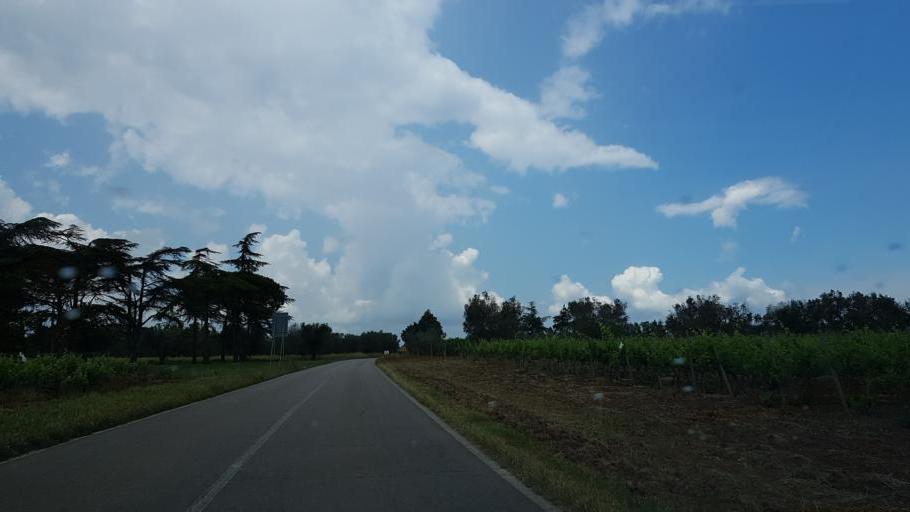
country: IT
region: Apulia
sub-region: Provincia di Brindisi
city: San Donaci
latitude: 40.4692
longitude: 17.9303
